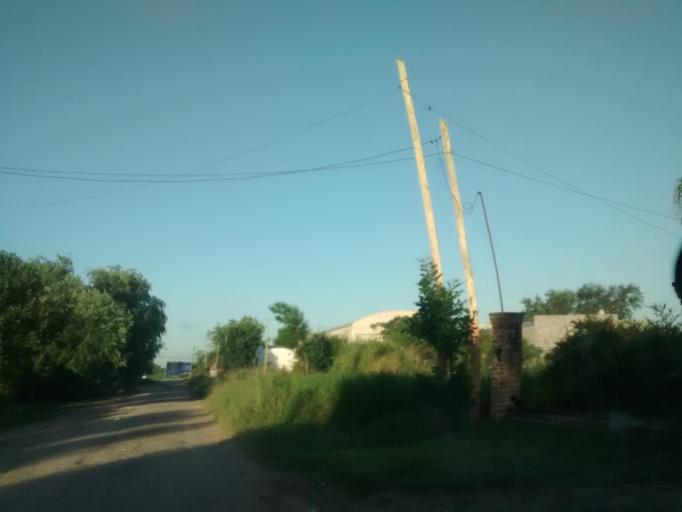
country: AR
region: Chaco
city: Fontana
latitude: -27.4336
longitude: -59.0232
